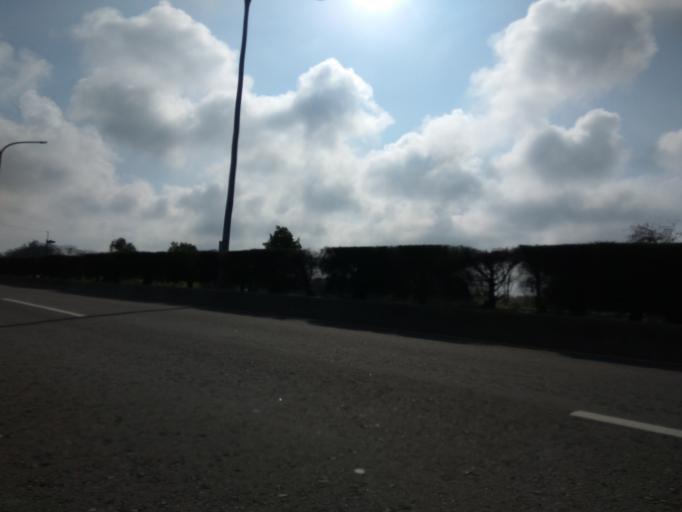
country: TW
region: Taiwan
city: Taoyuan City
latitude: 25.0723
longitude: 121.1731
